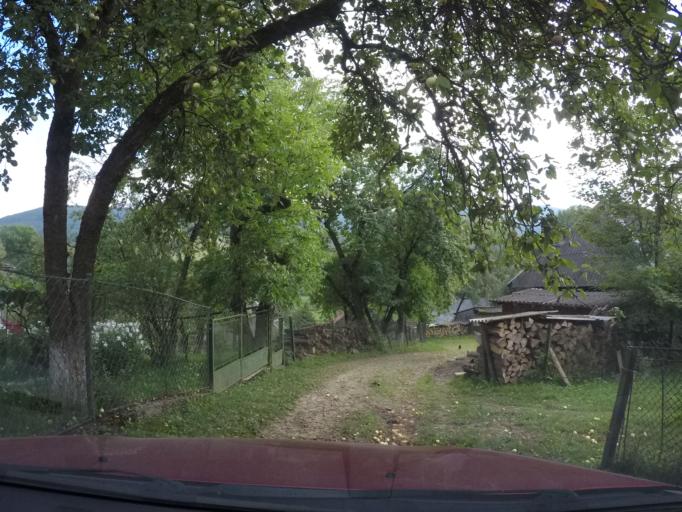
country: UA
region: Zakarpattia
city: Velykyi Bereznyi
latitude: 49.0301
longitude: 22.5905
